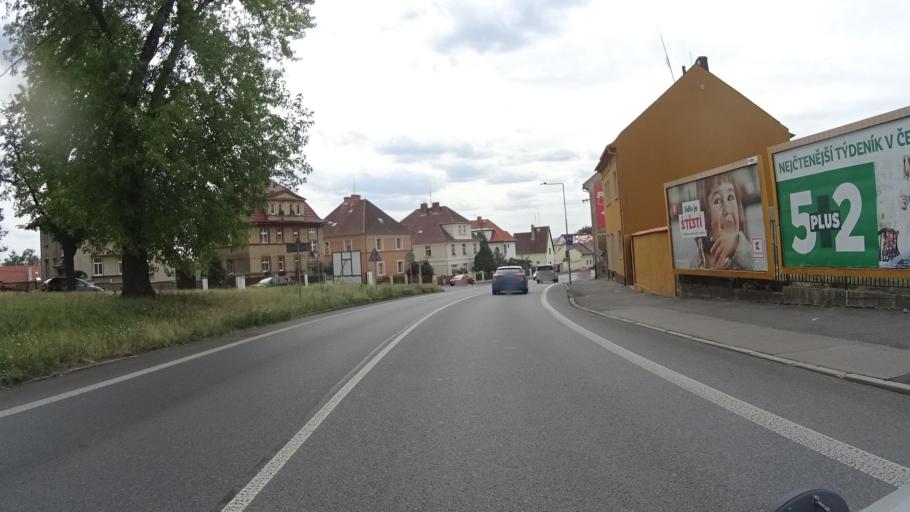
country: CZ
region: Ustecky
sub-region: Okres Litomerice
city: Litomerice
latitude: 50.5351
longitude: 14.1455
